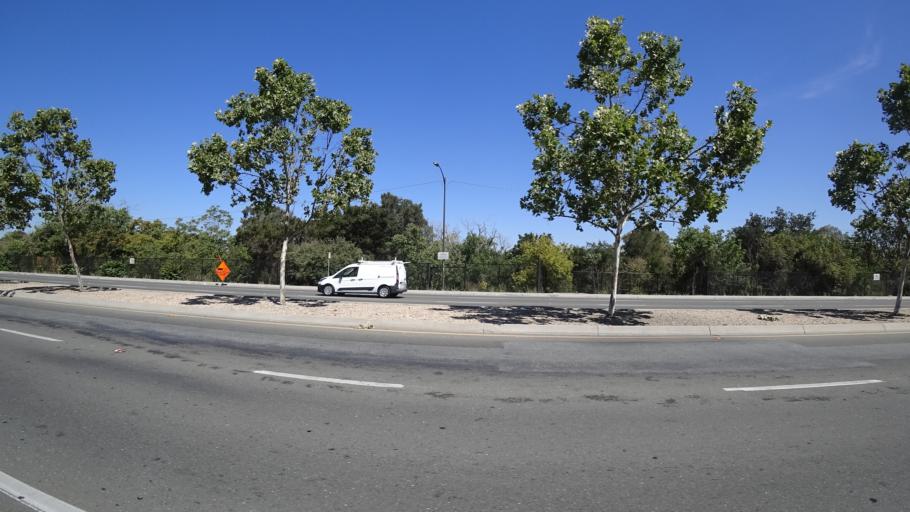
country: US
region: California
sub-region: Santa Clara County
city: San Jose
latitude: 37.3270
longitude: -121.8625
